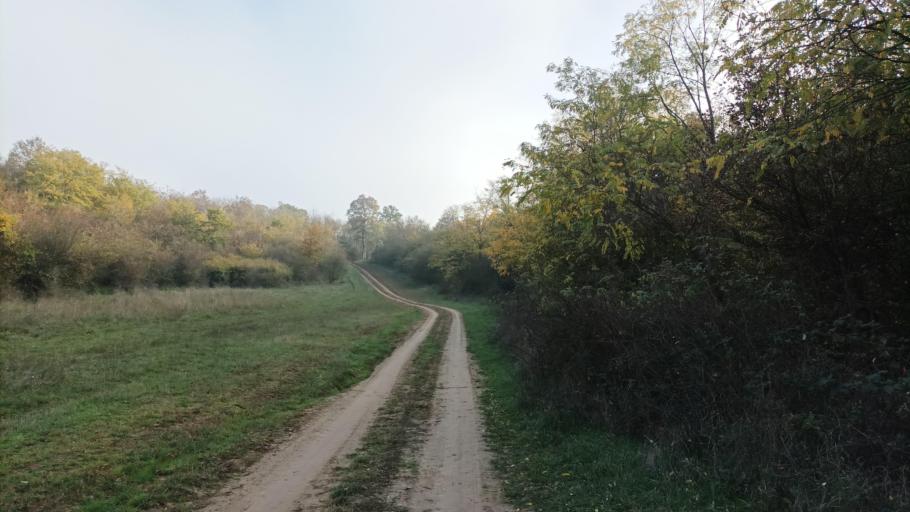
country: HU
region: Tolna
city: Szentgalpuszta
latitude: 46.3218
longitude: 18.6107
